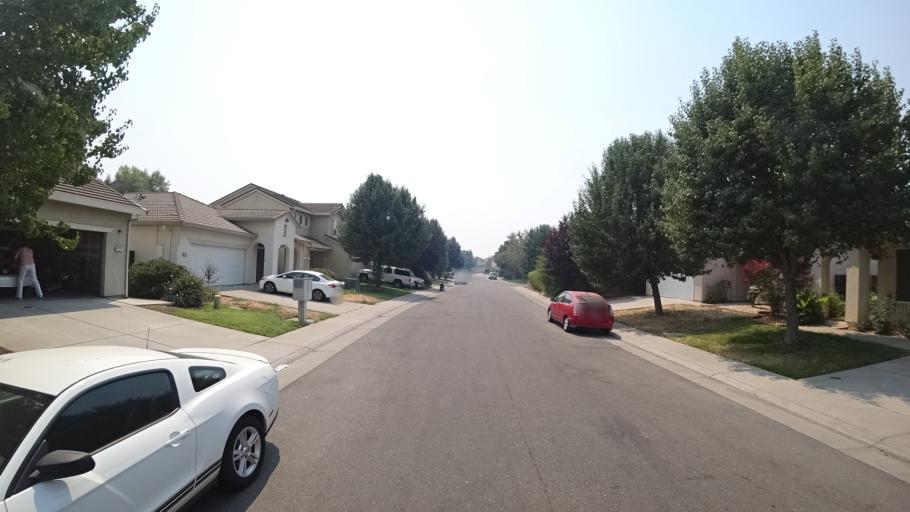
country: US
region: California
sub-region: Sacramento County
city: Laguna
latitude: 38.4022
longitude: -121.4344
